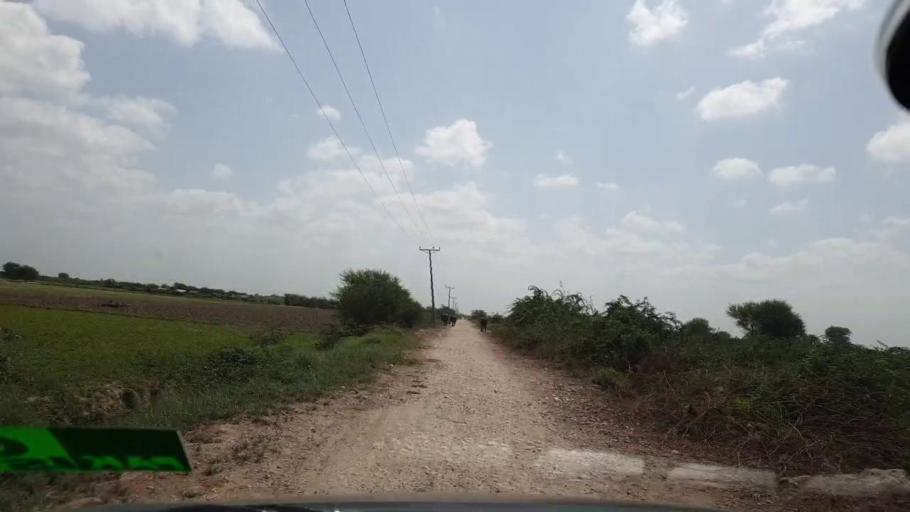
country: PK
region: Sindh
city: Kadhan
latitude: 24.6122
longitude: 69.1853
